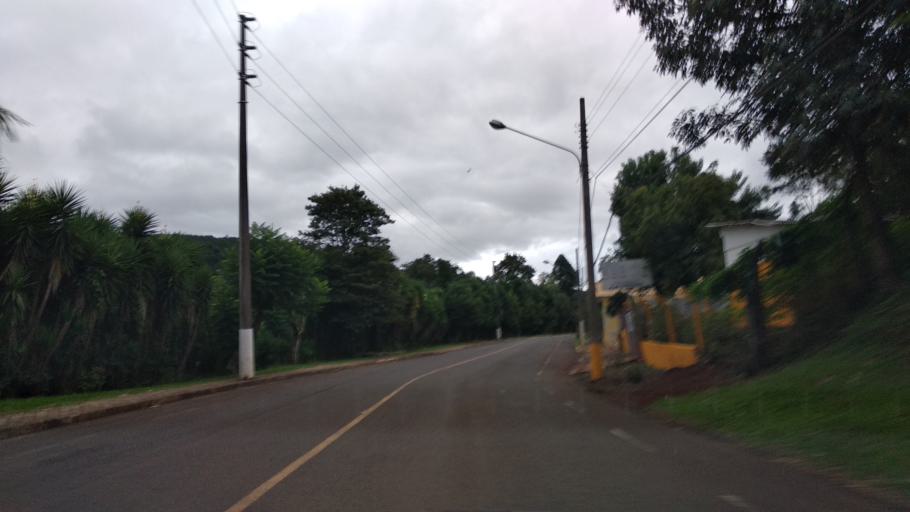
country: BR
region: Santa Catarina
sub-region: Videira
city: Videira
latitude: -27.0491
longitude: -51.2321
